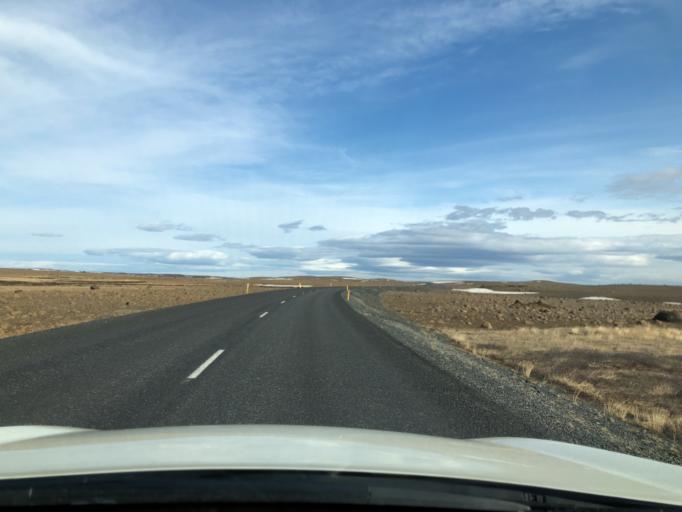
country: IS
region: Northeast
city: Husavik
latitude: 65.7814
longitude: -16.4407
